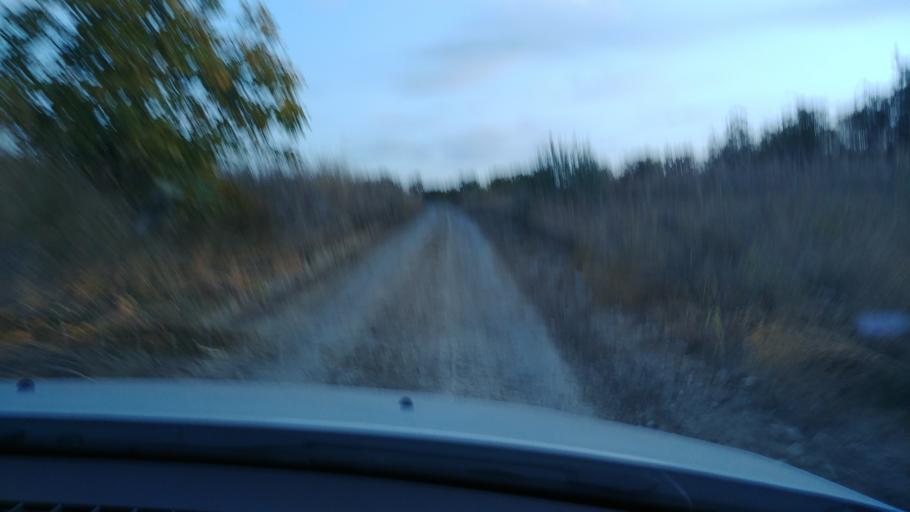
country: MD
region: Rezina
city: Saharna
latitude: 47.6847
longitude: 28.9079
